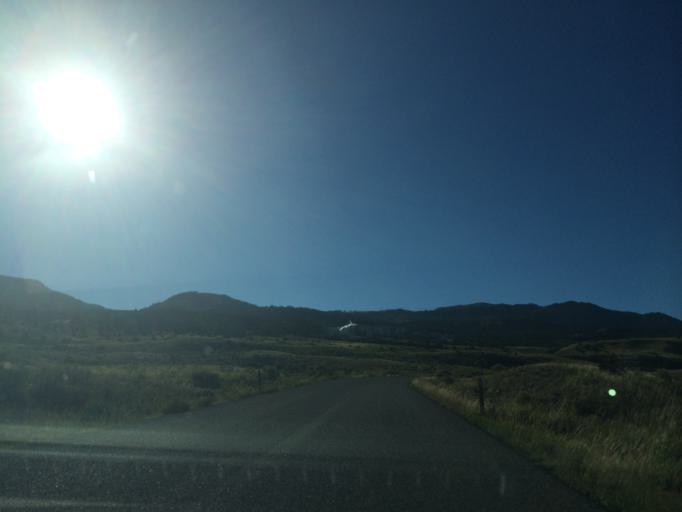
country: US
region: Montana
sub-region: Gallatin County
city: West Yellowstone
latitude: 44.9651
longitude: -110.6892
